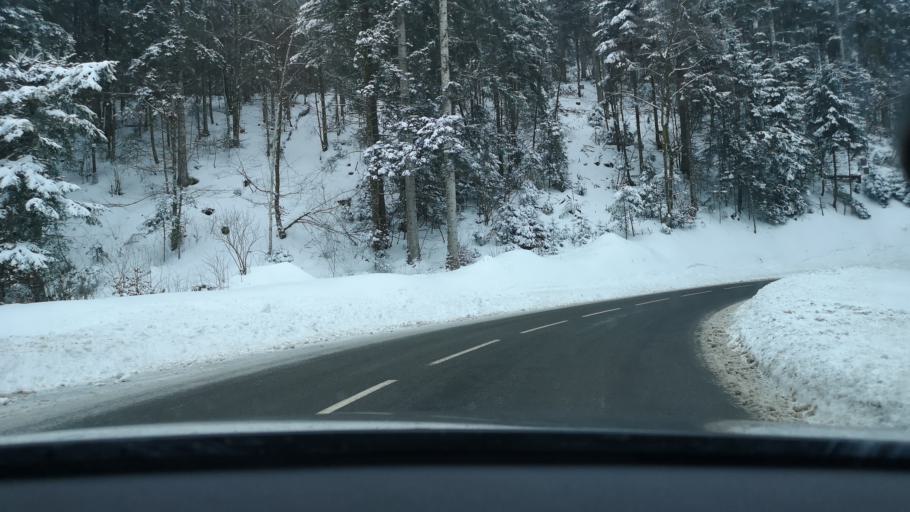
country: FR
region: Rhone-Alpes
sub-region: Departement de l'Ain
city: Oyonnax
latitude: 46.2467
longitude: 5.7091
